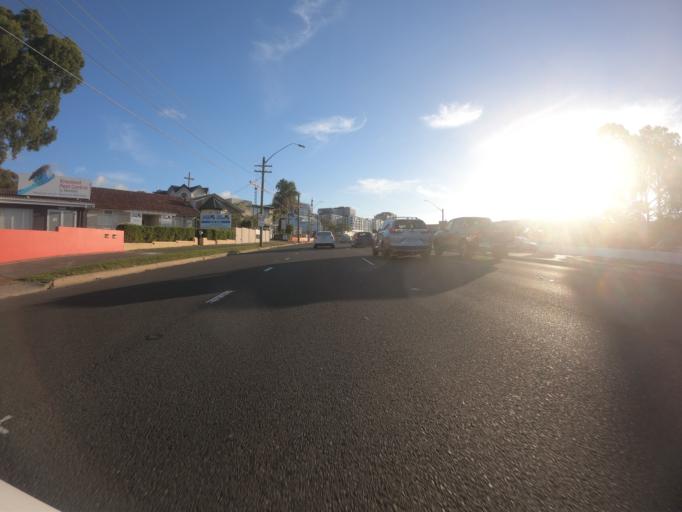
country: AU
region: New South Wales
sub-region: Sutherland Shire
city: Gymea
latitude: -34.0317
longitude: 151.0774
